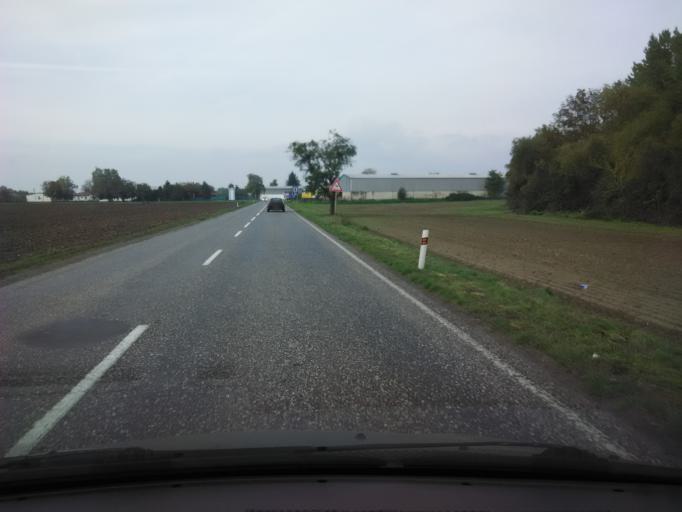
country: SK
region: Nitriansky
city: Levice
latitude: 48.1910
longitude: 18.5134
